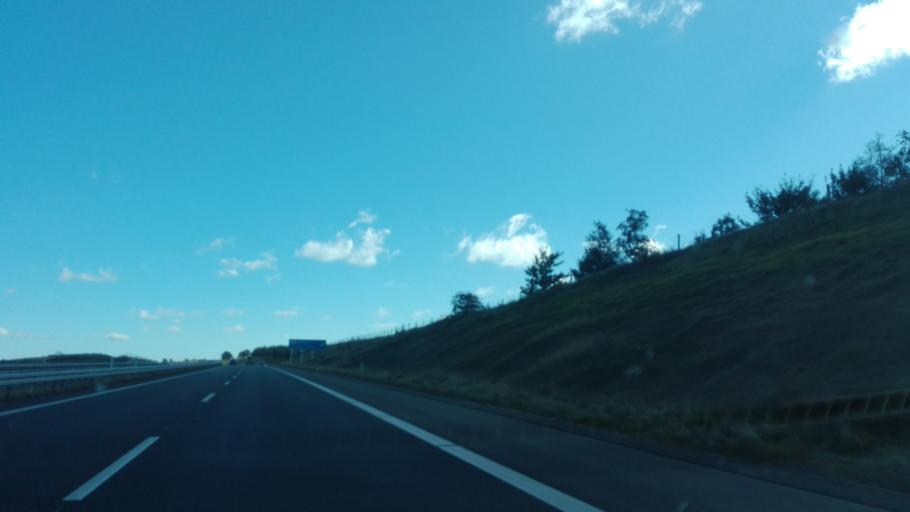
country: DK
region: Central Jutland
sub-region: Silkeborg Kommune
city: Svejbaek
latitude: 56.1558
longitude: 9.6254
